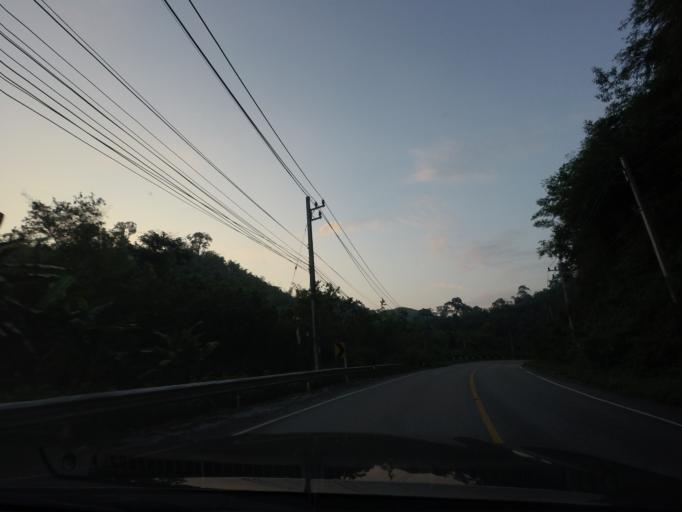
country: TH
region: Nan
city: Na Noi
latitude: 18.4227
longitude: 100.6976
